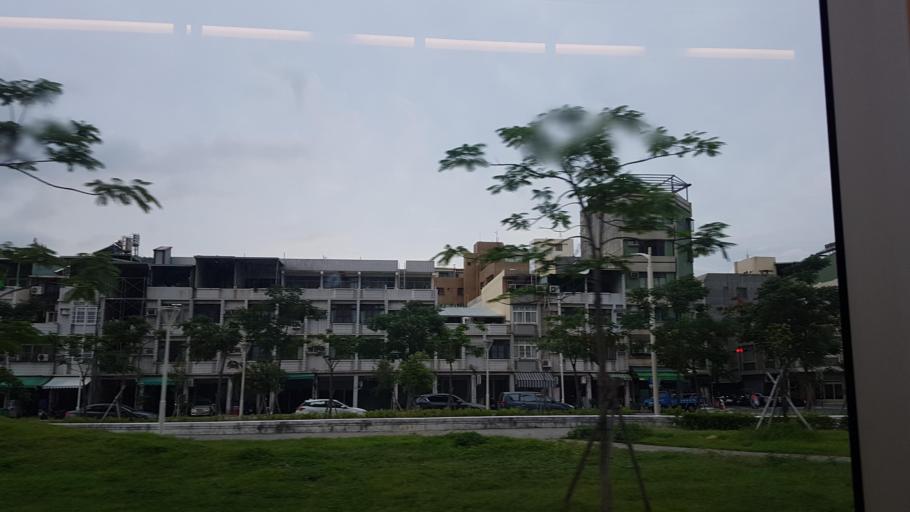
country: TW
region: Kaohsiung
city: Kaohsiung
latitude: 22.6495
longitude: 120.2815
